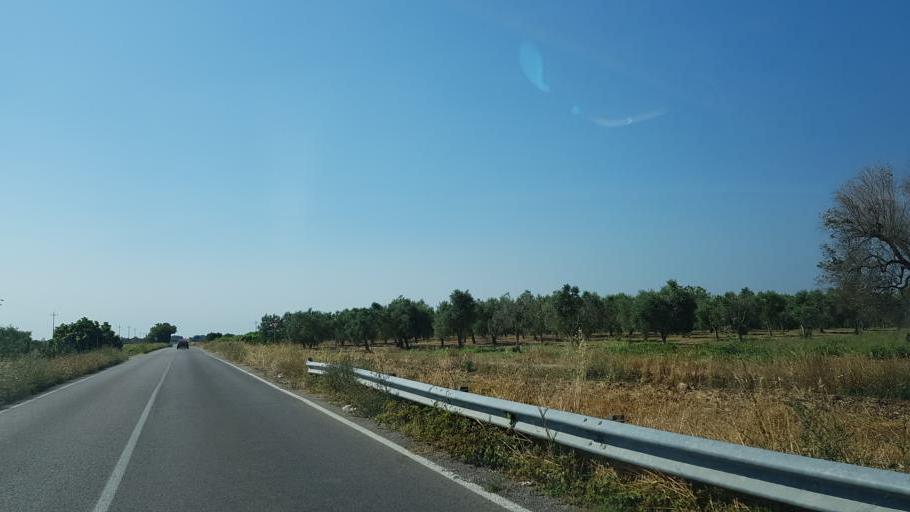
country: IT
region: Apulia
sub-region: Provincia di Lecce
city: Guagnano
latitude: 40.4254
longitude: 17.9461
